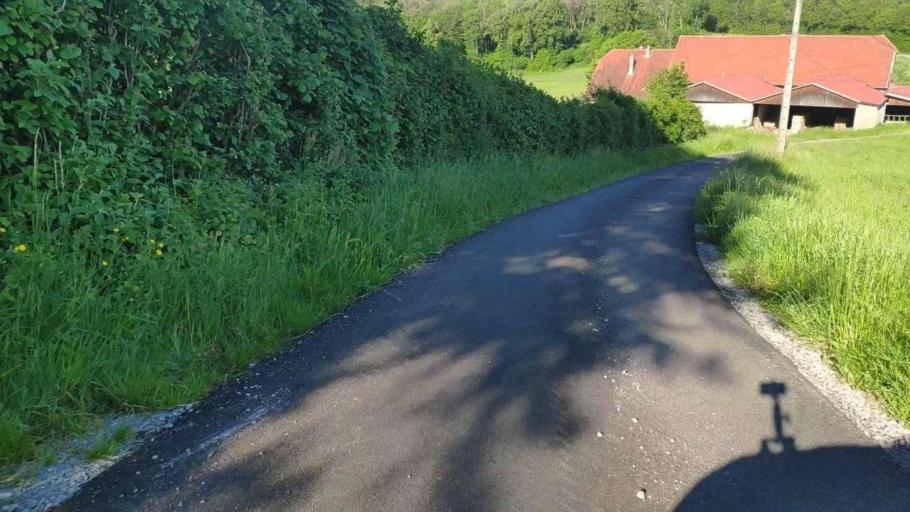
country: FR
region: Franche-Comte
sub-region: Departement du Jura
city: Perrigny
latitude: 46.7230
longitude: 5.6149
